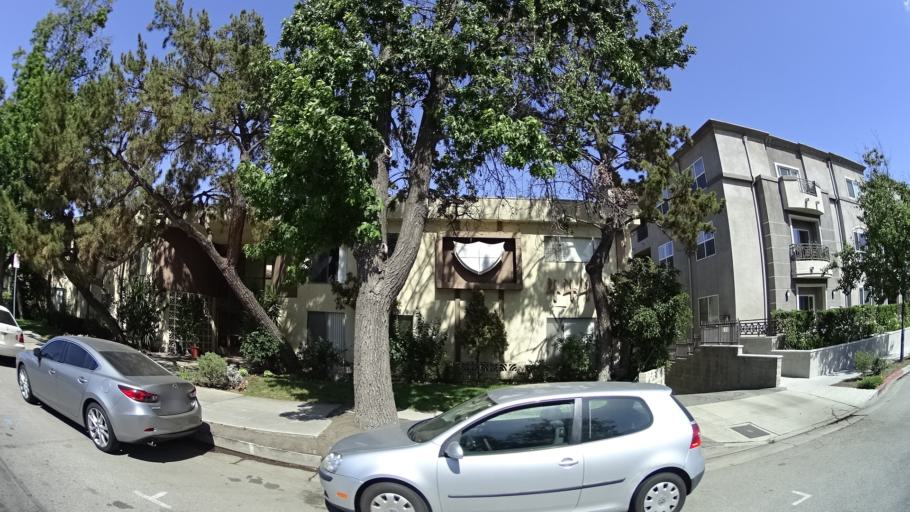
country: US
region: California
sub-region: Los Angeles County
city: North Hollywood
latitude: 34.1516
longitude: -118.4052
